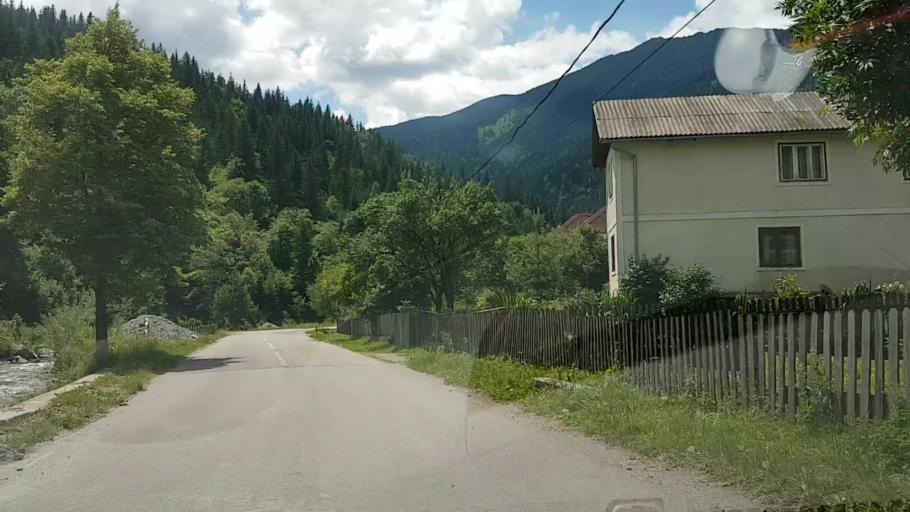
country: RO
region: Suceava
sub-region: Comuna Crucea
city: Crucea
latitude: 47.4008
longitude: 25.5696
